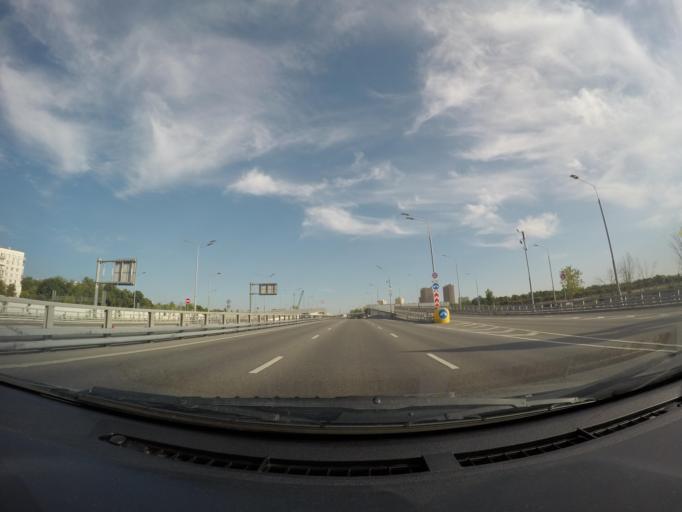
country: RU
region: Moscow
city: Likhobory
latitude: 55.8416
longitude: 37.5638
